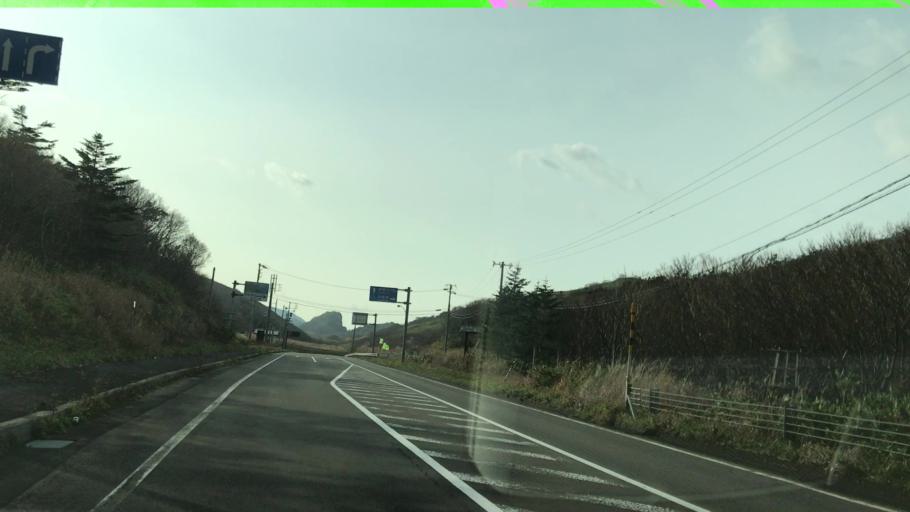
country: JP
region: Hokkaido
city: Iwanai
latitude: 43.3248
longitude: 140.3640
